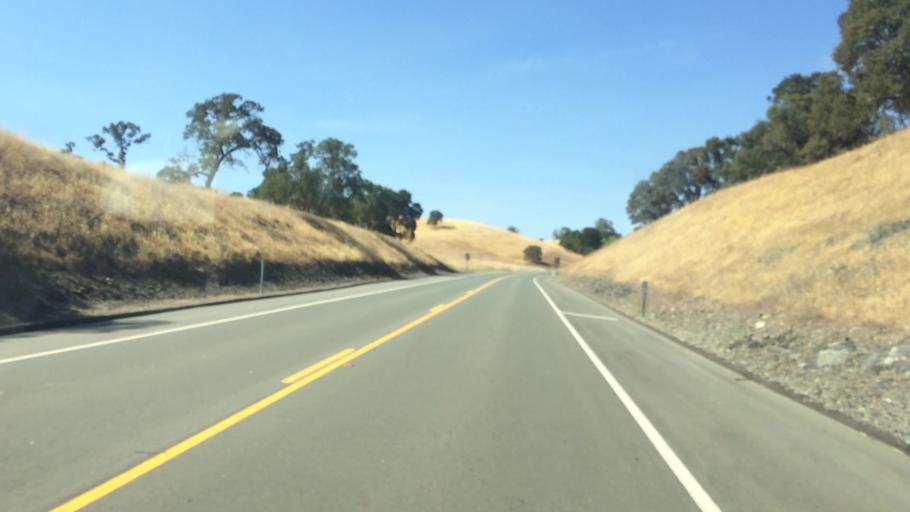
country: US
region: California
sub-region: Amador County
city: Plymouth
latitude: 38.4351
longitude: -120.8773
